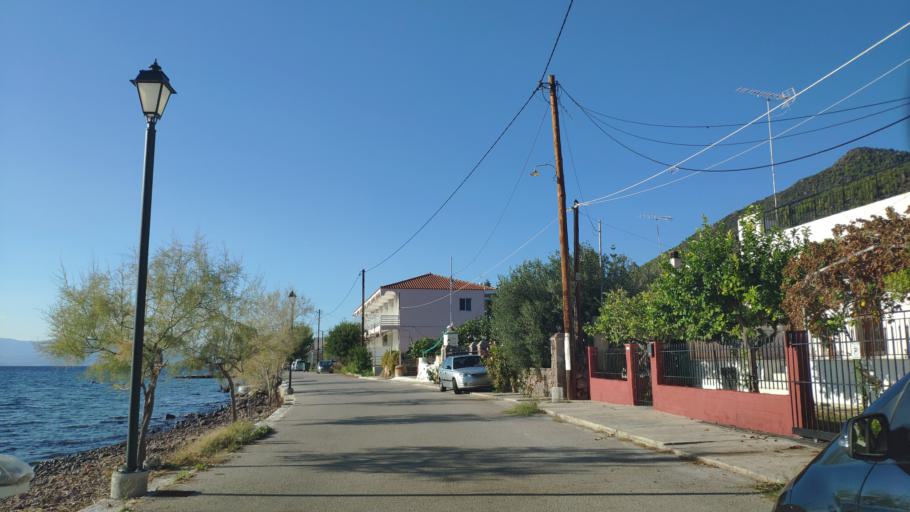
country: GR
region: Attica
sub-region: Nomos Piraios
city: Megalochori
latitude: 37.5888
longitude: 23.3457
